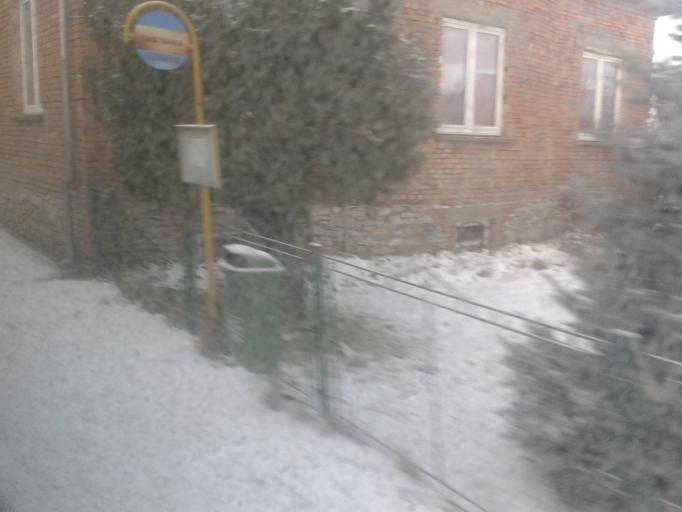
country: CZ
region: Olomoucky
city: Smrzice
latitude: 49.5013
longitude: 17.0992
